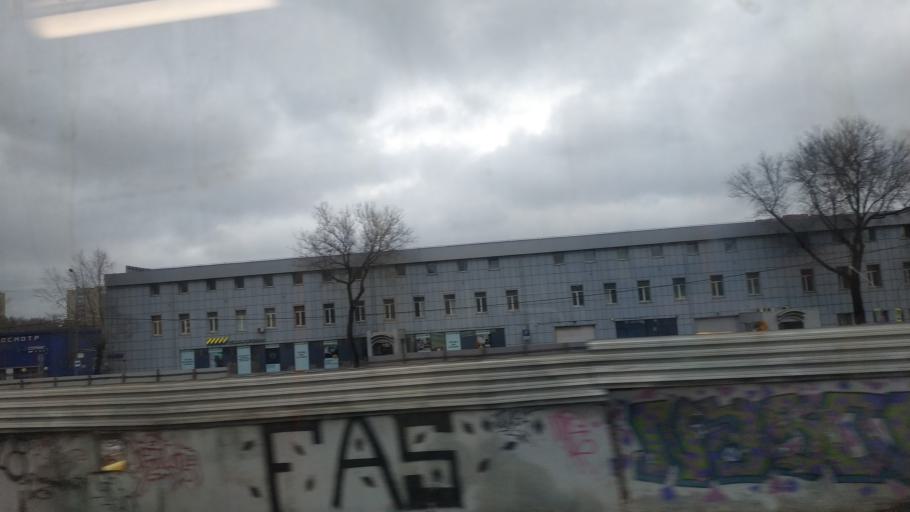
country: RU
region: Moscow
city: Lefortovo
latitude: 55.7289
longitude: 37.7086
